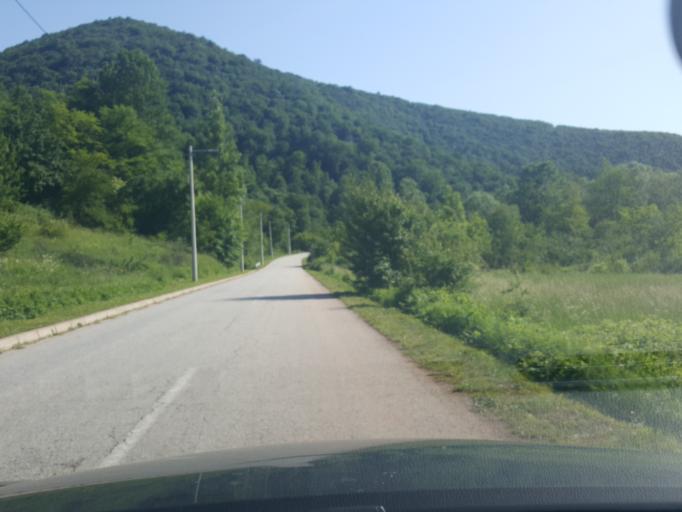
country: RS
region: Central Serbia
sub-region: Nisavski Okrug
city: Razanj
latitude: 43.8613
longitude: 21.6250
